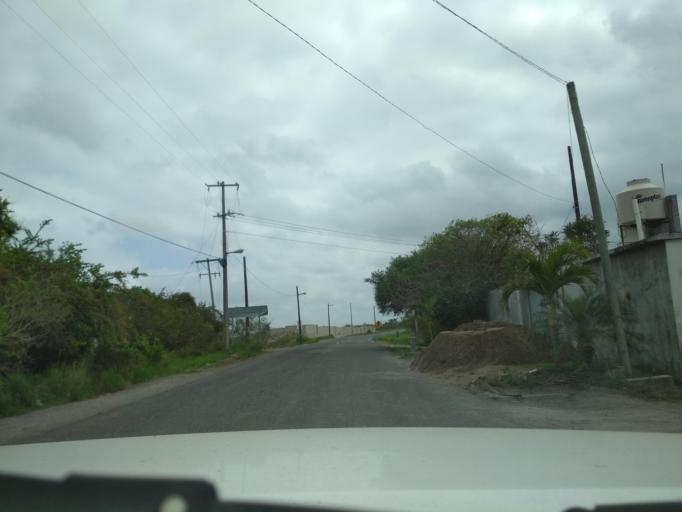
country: MX
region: Veracruz
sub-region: Veracruz
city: Delfino Victoria (Santa Fe)
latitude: 19.2452
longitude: -96.2579
